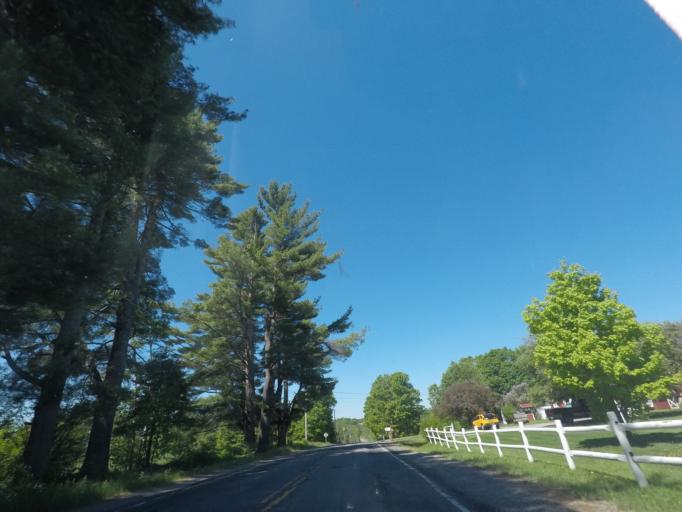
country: US
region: Maine
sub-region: Kennebec County
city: Gardiner
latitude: 44.2280
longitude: -69.8337
